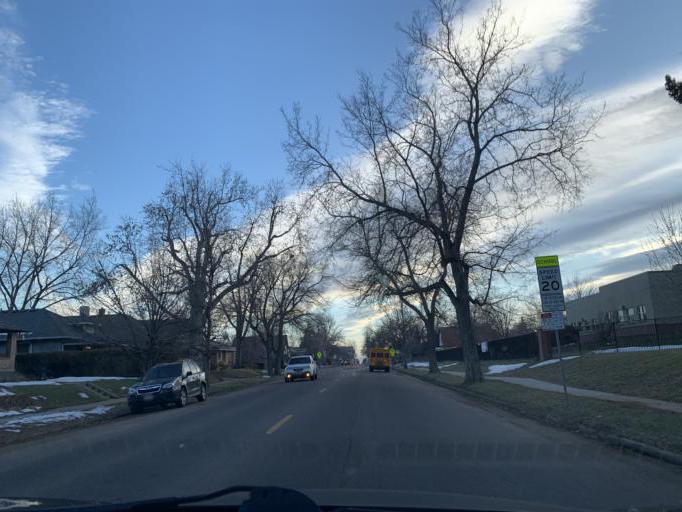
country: US
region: Colorado
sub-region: Adams County
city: Berkley
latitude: 39.7742
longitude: -105.0346
